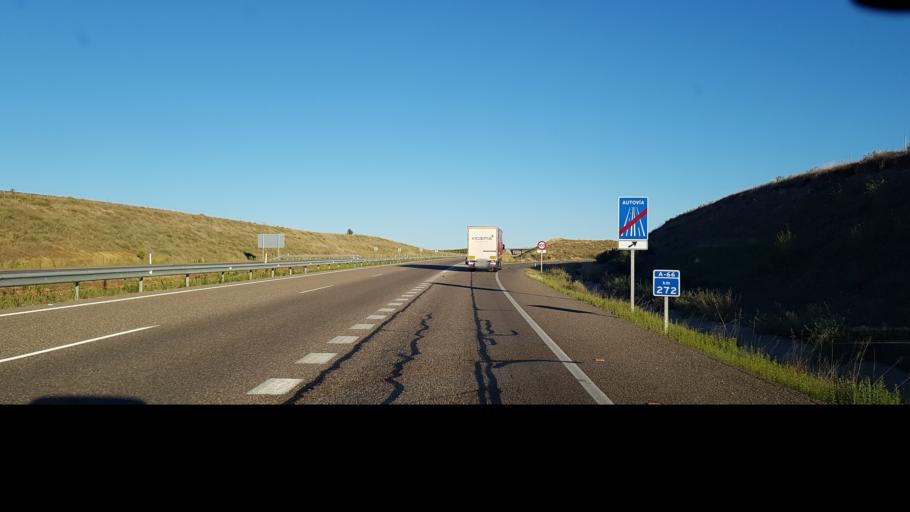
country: ES
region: Castille and Leon
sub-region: Provincia de Zamora
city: Valcabado
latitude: 41.5544
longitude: -5.7391
